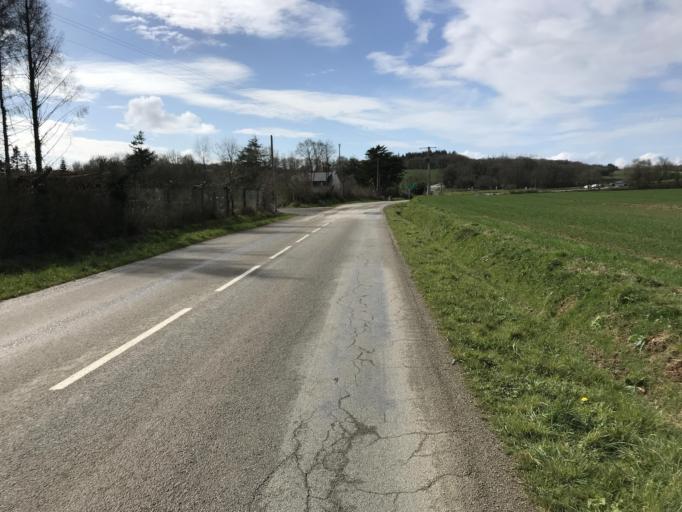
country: FR
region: Brittany
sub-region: Departement du Finistere
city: Daoulas
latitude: 48.3777
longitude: -4.2703
